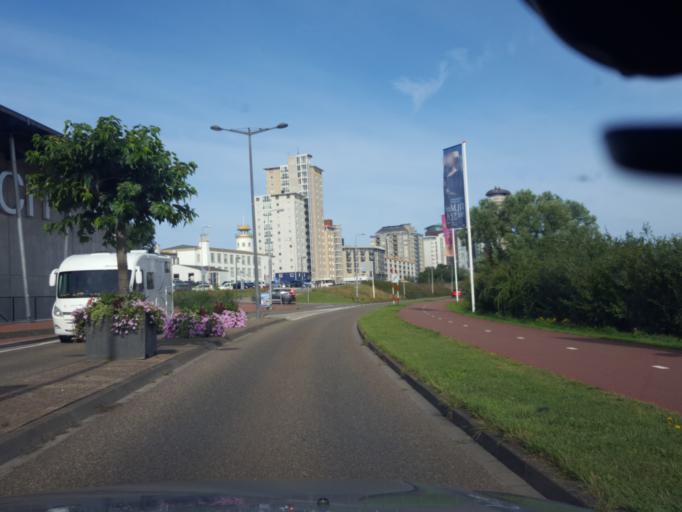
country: NL
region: Zeeland
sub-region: Gemeente Vlissingen
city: Vlissingen
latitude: 51.4451
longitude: 3.5684
